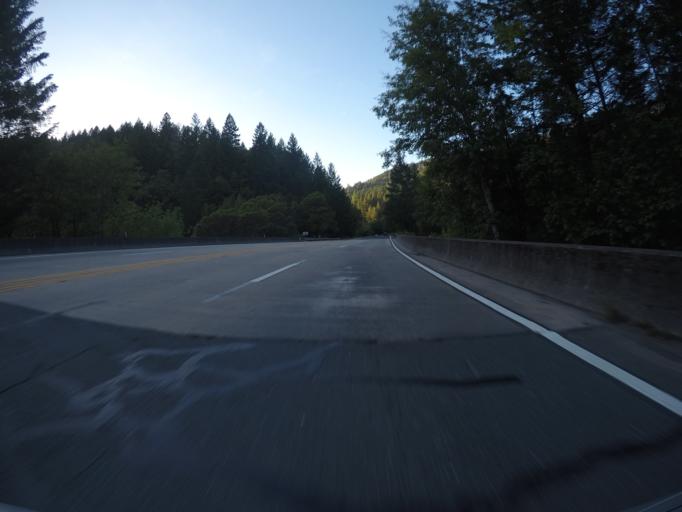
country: US
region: California
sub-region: Mendocino County
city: Laytonville
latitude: 39.5813
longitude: -123.4441
